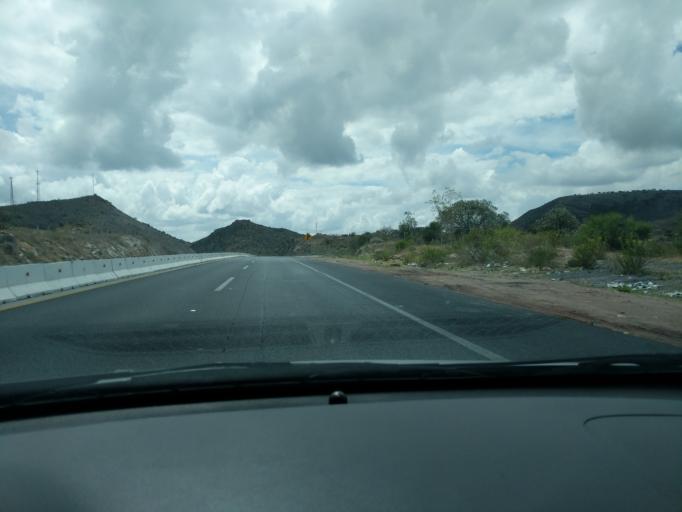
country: MX
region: San Luis Potosi
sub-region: Mexquitic de Carmona
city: Cerrito de Jaral
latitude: 22.2529
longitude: -101.1146
